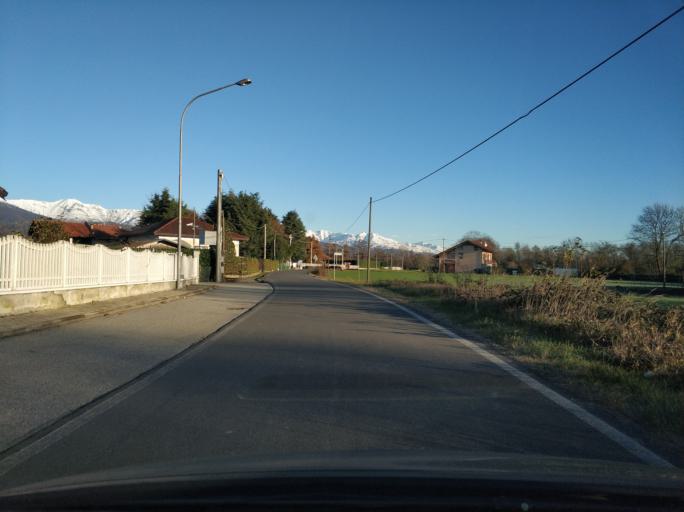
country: IT
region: Piedmont
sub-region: Provincia di Torino
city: Villanova Canavese
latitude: 45.2313
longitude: 7.5415
